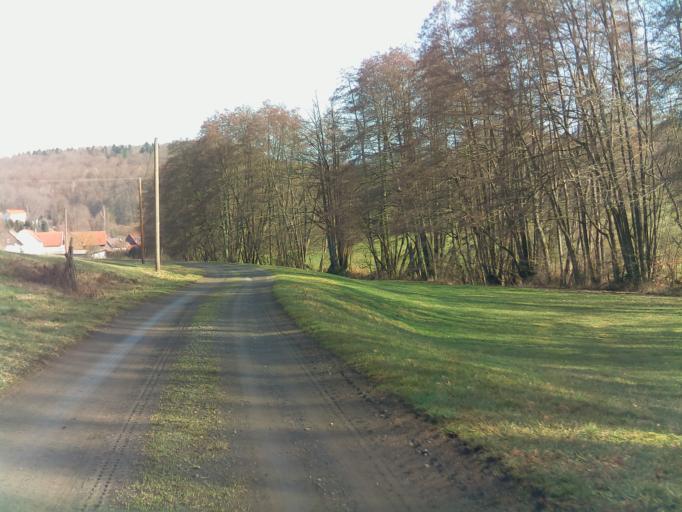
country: DE
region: Rheinland-Pfalz
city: Langenbach
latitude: 49.4881
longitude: 7.3268
